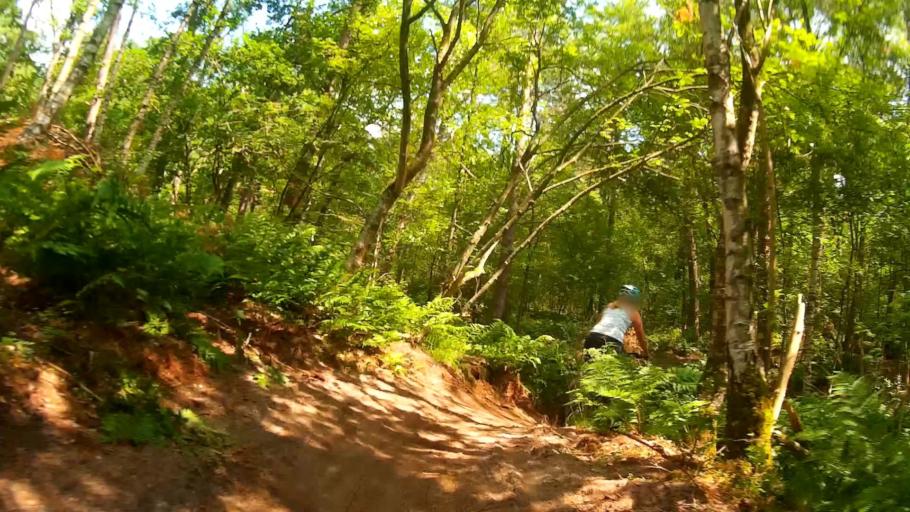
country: NL
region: North Holland
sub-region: Gemeente Hilversum
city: Hilversum
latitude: 52.2024
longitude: 5.2163
